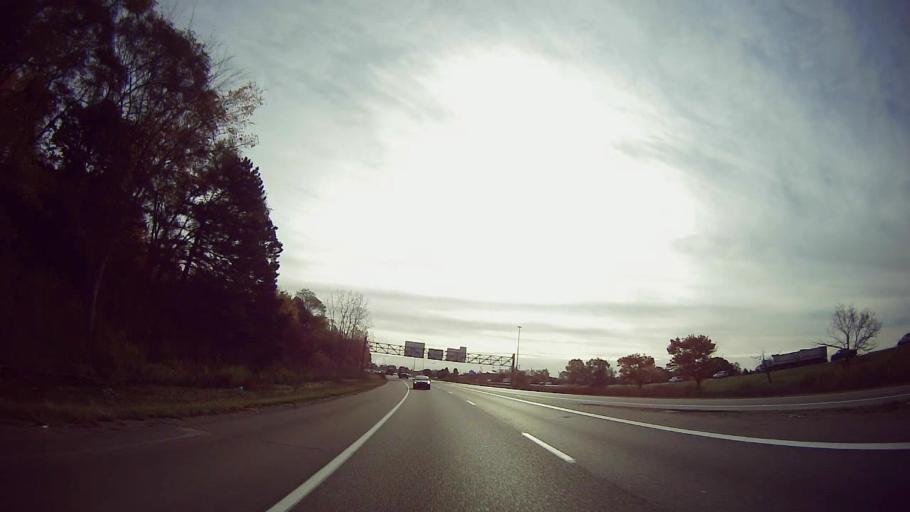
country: US
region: Michigan
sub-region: Wayne County
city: Plymouth
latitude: 42.3857
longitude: -83.4300
